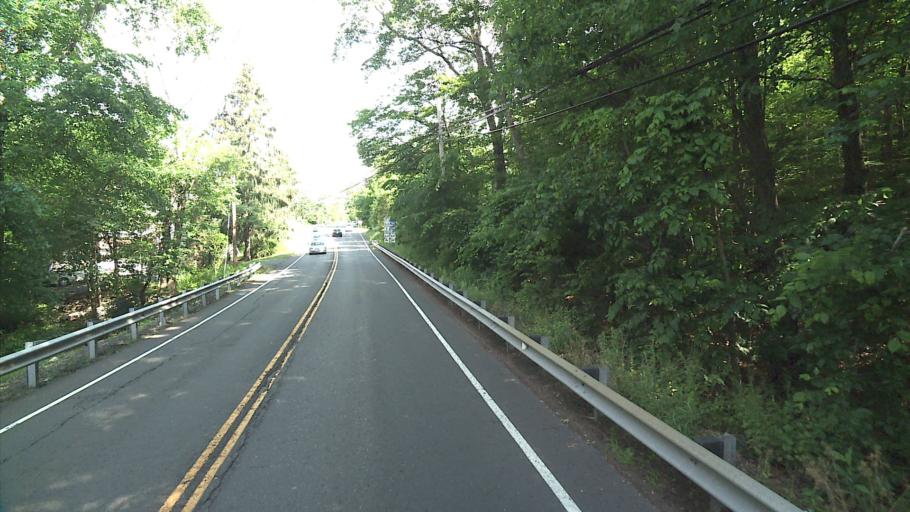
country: US
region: Connecticut
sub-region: New Haven County
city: Middlebury
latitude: 41.5398
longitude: -73.0885
